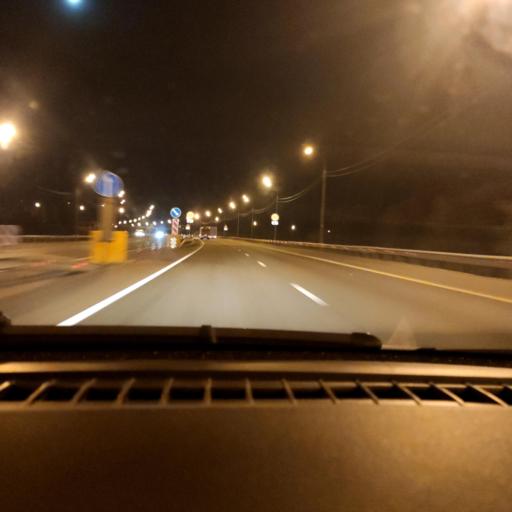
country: RU
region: Lipetsk
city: Khlevnoye
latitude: 52.2412
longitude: 39.0688
